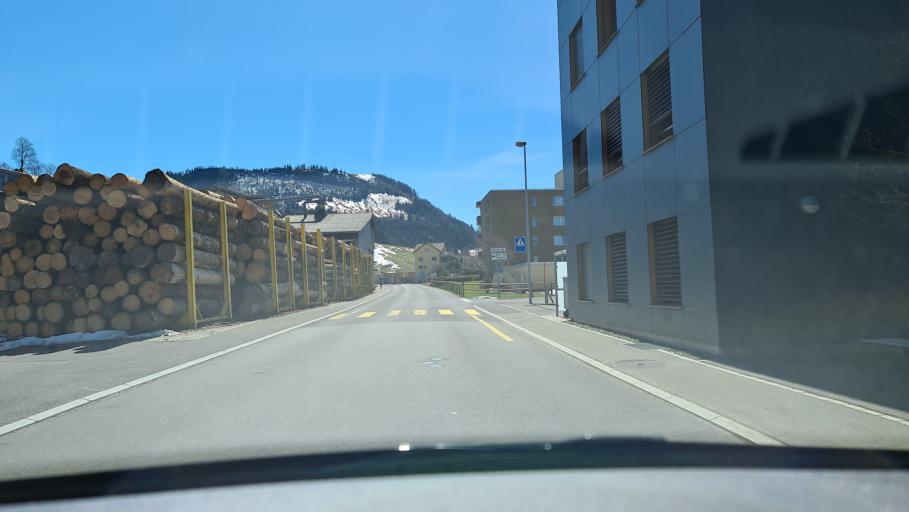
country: CH
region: Schwyz
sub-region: Bezirk Einsiedeln
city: Einsiedeln
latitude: 47.1234
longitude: 8.7428
